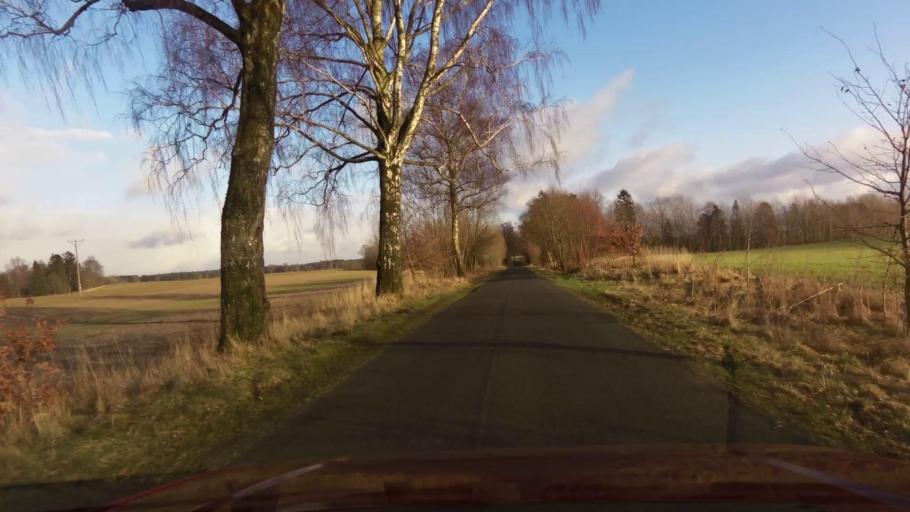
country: PL
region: West Pomeranian Voivodeship
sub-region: Koszalin
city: Koszalin
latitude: 54.0730
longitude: 16.1366
